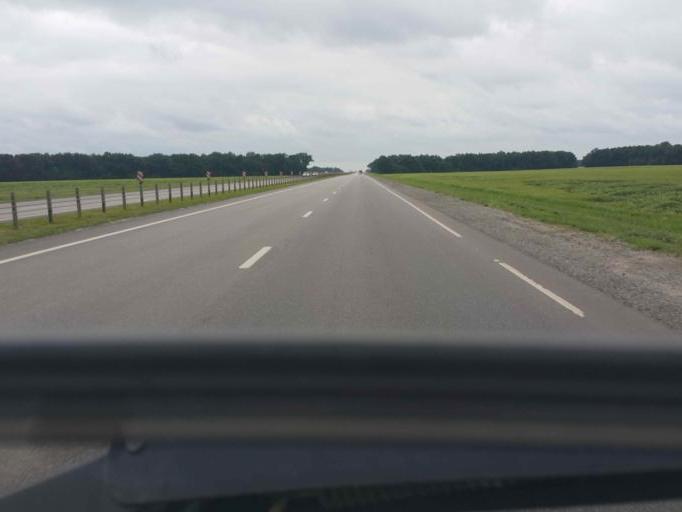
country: RU
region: Tambov
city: Zavoronezhskoye
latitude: 52.8932
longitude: 40.6890
